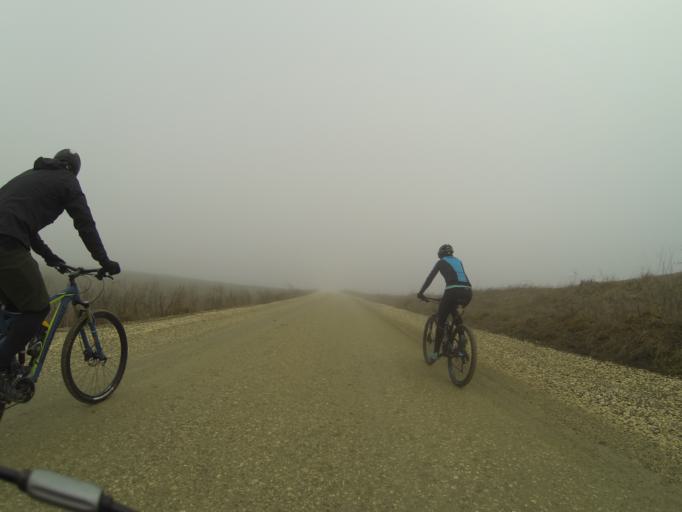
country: RO
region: Mehedinti
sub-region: Comuna Balacita
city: Gvardinita
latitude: 44.4274
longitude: 23.1307
